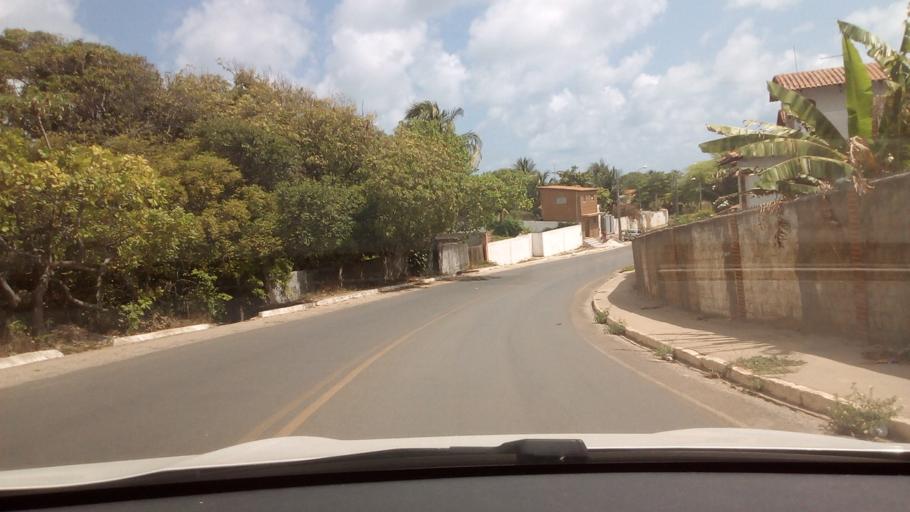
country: BR
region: Paraiba
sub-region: Conde
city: Conde
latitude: -7.2905
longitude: -34.8065
